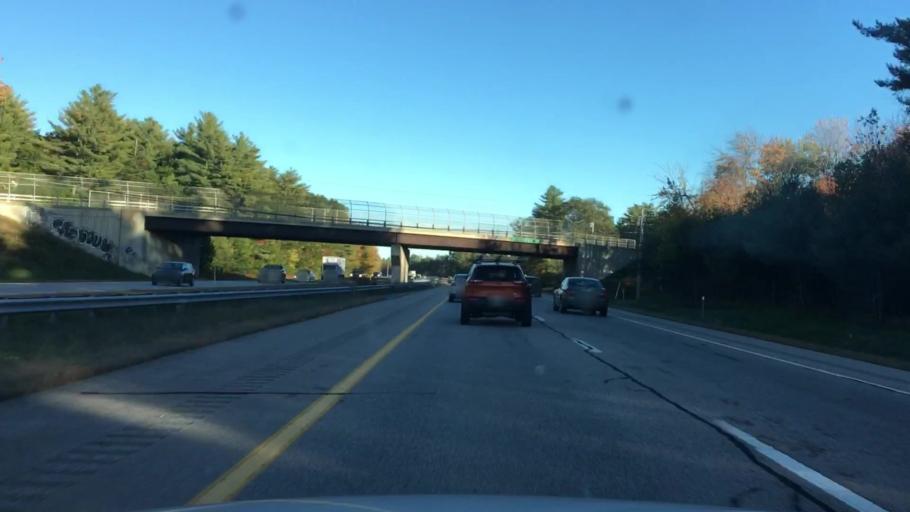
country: US
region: New Hampshire
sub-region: Rockingham County
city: Fremont
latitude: 43.0271
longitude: -71.1181
